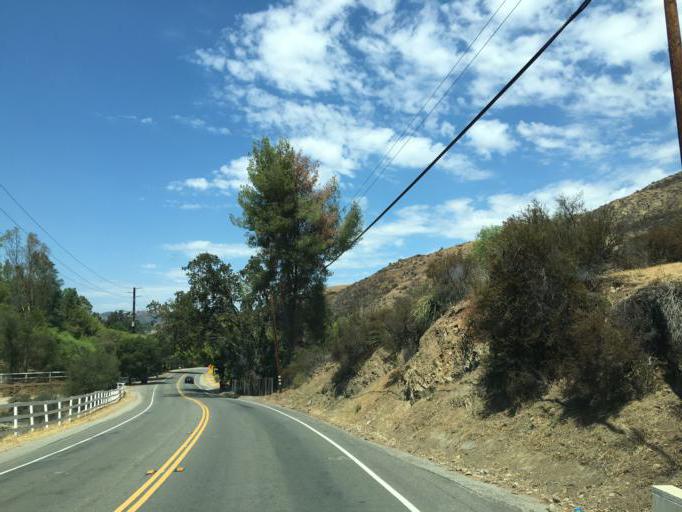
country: US
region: California
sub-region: Los Angeles County
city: Agoura
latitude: 34.1356
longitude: -118.7547
